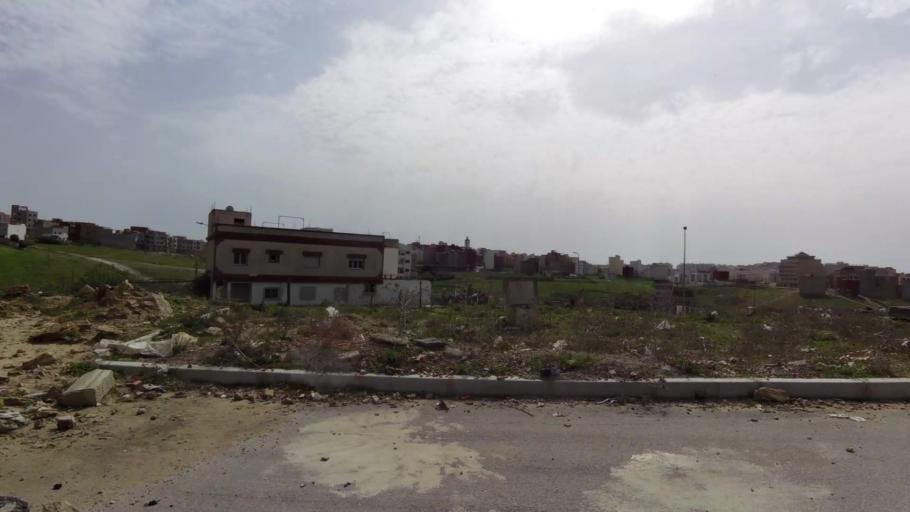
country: MA
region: Tanger-Tetouan
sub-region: Tanger-Assilah
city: Tangier
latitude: 35.7392
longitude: -5.8388
